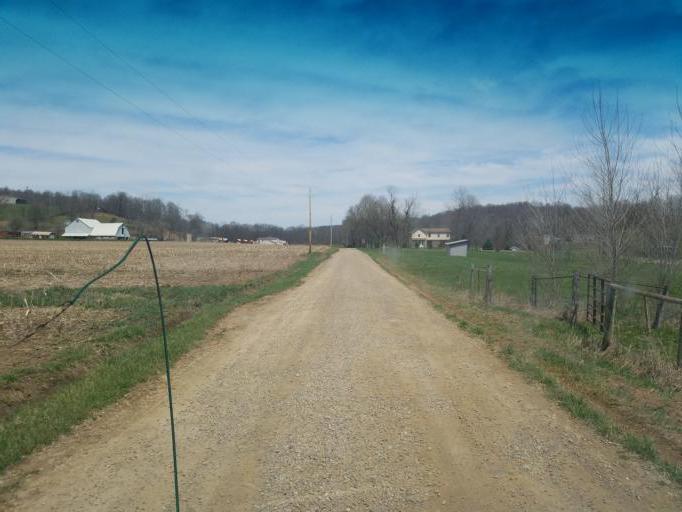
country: US
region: Ohio
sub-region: Knox County
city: Danville
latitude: 40.5369
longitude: -82.3237
